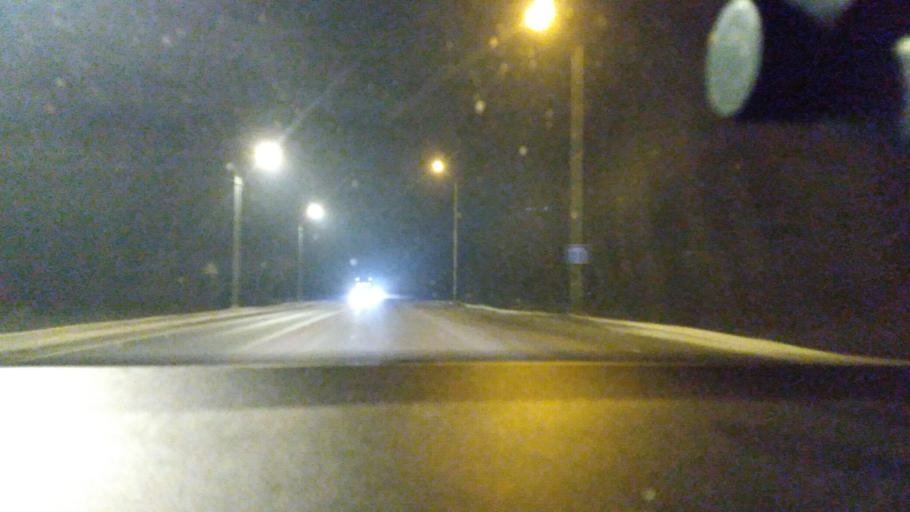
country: RU
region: Moskovskaya
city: Yegor'yevsk
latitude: 55.4193
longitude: 39.0417
